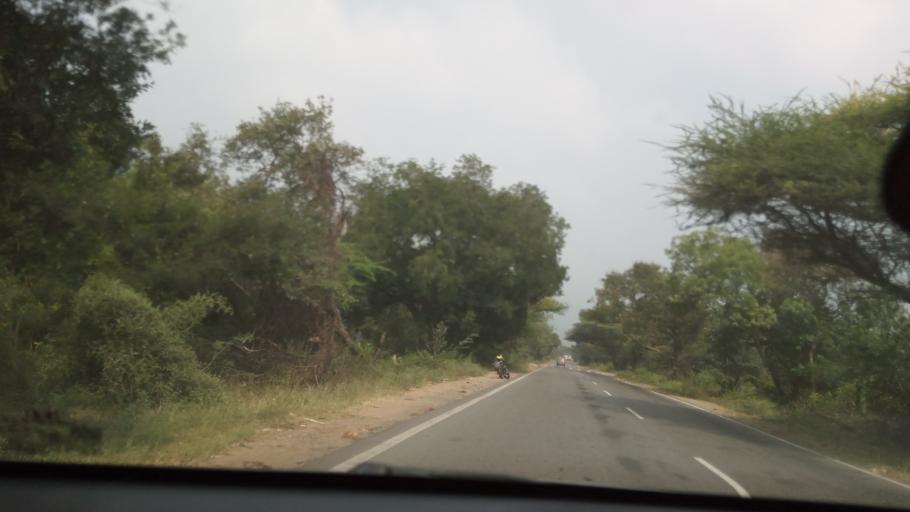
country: IN
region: Tamil Nadu
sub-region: Erode
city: Sathyamangalam
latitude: 11.5598
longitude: 77.1364
